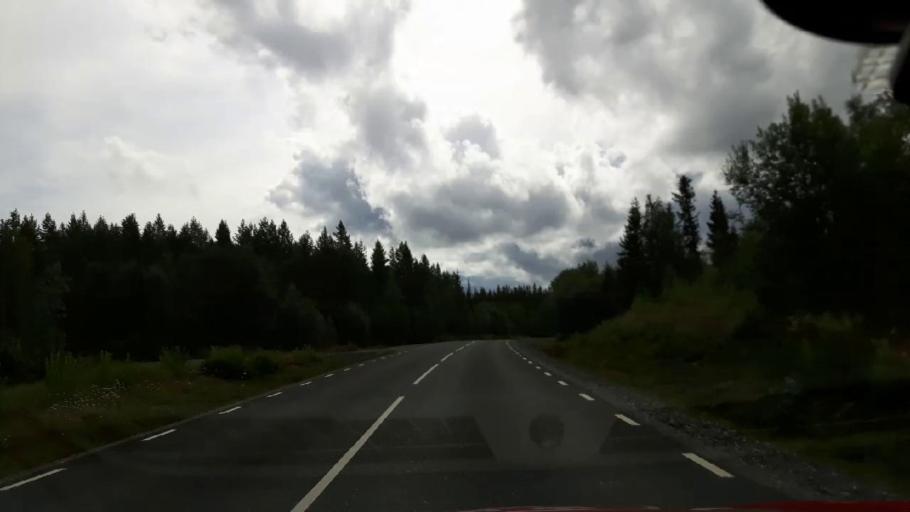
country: NO
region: Nord-Trondelag
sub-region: Lierne
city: Sandvika
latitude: 64.5997
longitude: 14.1207
